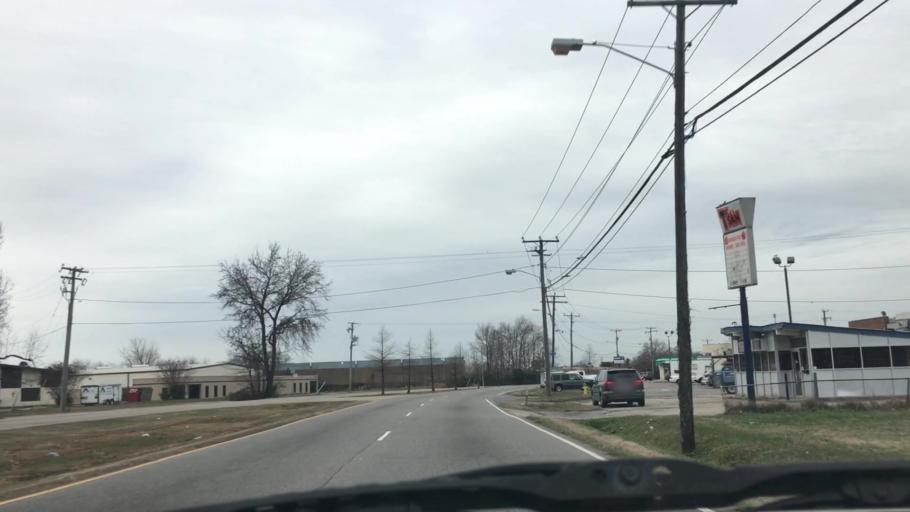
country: US
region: Virginia
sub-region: City of Norfolk
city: Norfolk
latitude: 36.8676
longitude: -76.2303
